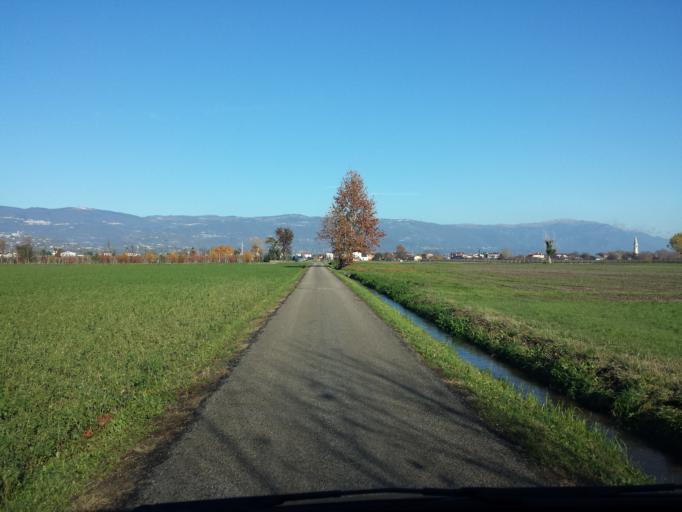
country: IT
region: Veneto
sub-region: Provincia di Vicenza
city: Sandrigo
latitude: 45.6807
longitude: 11.5970
